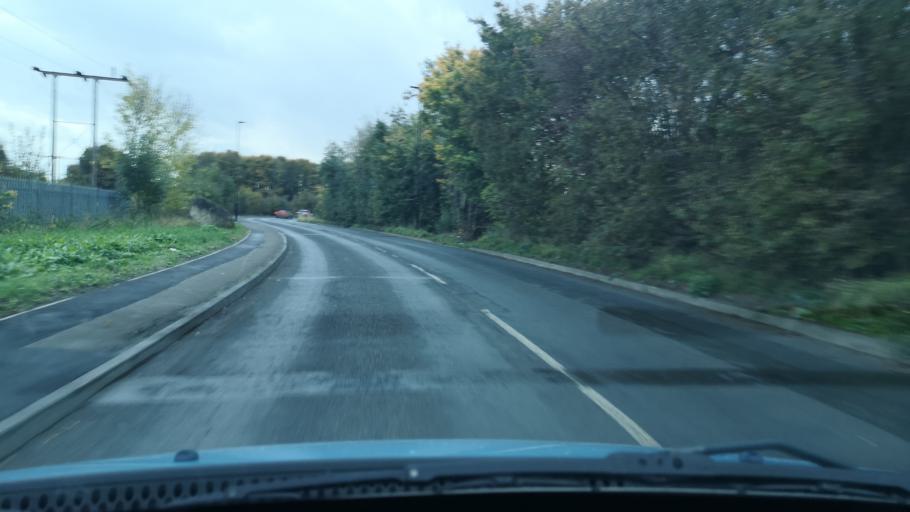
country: GB
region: England
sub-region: Doncaster
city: Askern
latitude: 53.6192
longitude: -1.1599
